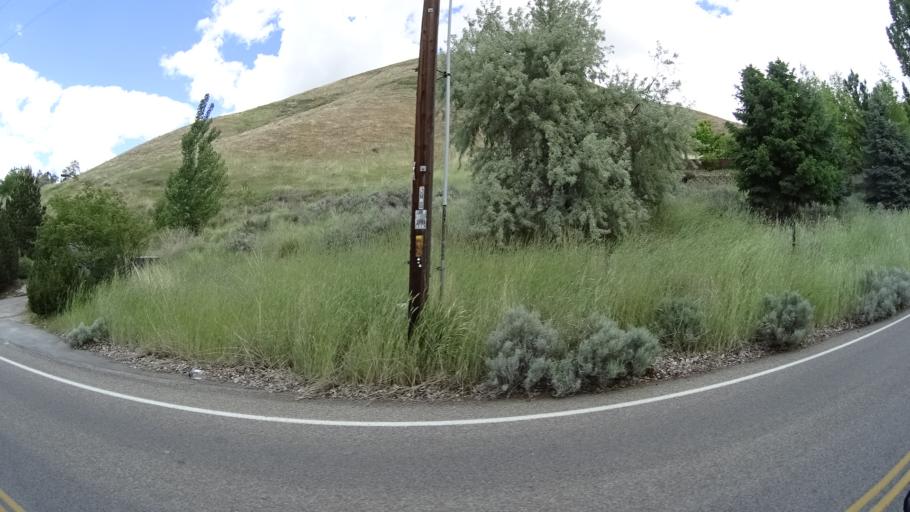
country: US
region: Idaho
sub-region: Ada County
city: Garden City
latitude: 43.6591
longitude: -116.2316
